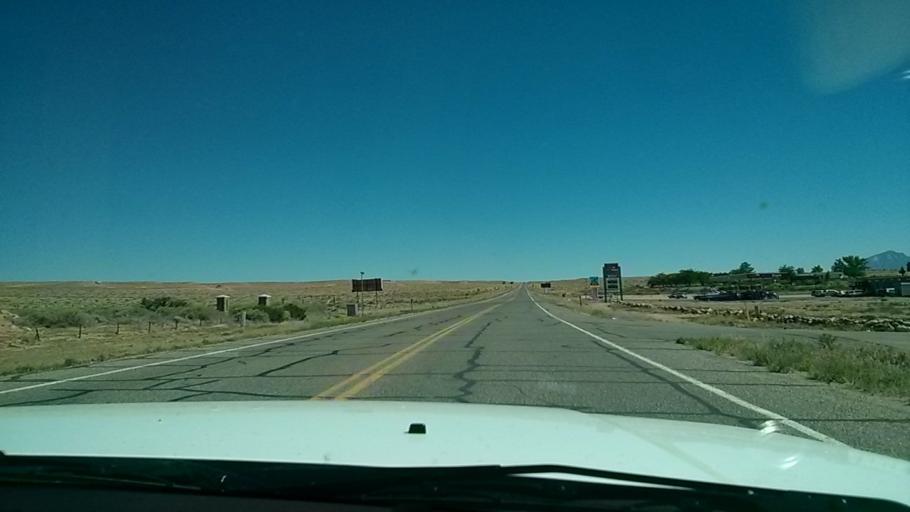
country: US
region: Utah
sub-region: Emery County
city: Ferron
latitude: 38.3720
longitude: -110.7038
